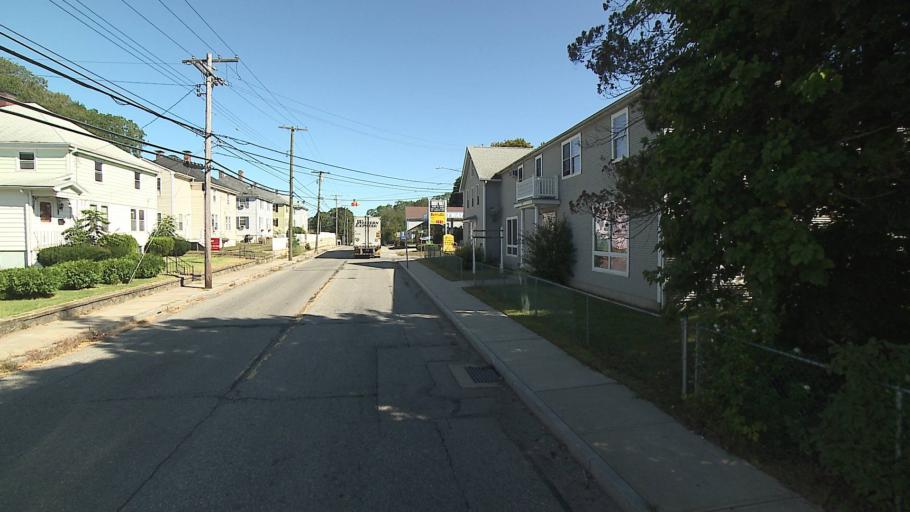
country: US
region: Connecticut
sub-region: New London County
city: Jewett City
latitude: 41.6134
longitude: -71.9794
